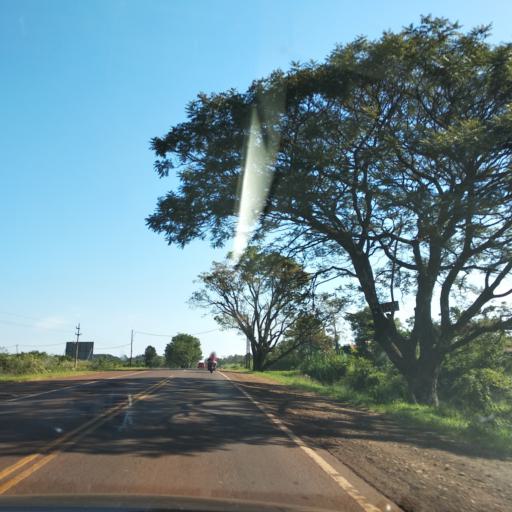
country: AR
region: Misiones
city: Jardin America
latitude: -27.0600
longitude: -55.2594
